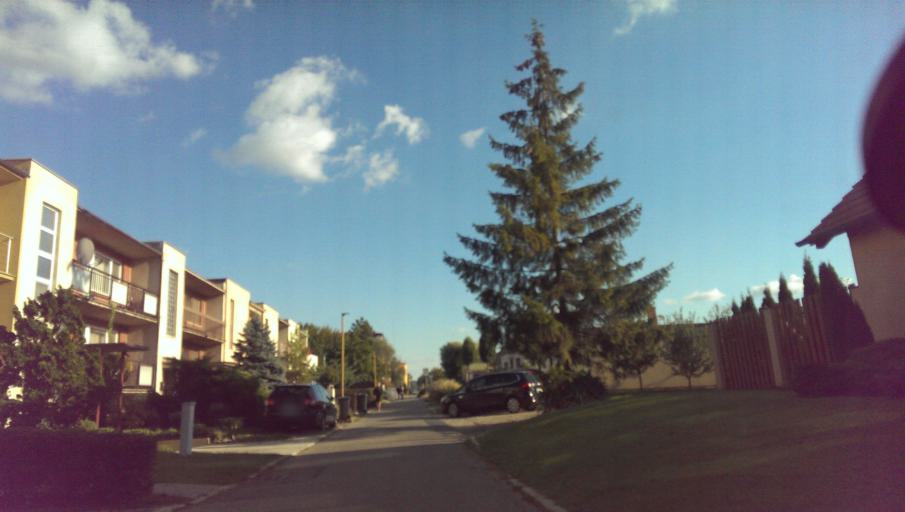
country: CZ
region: Zlin
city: Kunovice
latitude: 49.0609
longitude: 17.4779
